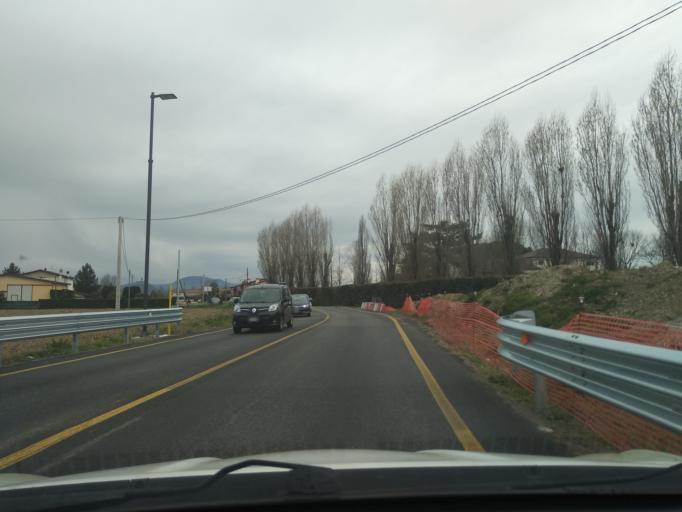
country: IT
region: Veneto
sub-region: Provincia di Padova
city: Rubano
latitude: 45.4167
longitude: 11.7902
